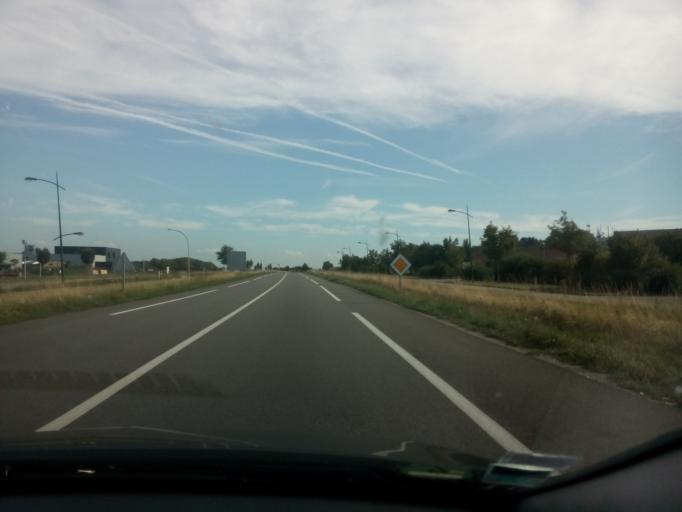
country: FR
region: Alsace
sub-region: Departement du Bas-Rhin
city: Wissembourg
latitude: 49.0207
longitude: 7.9658
